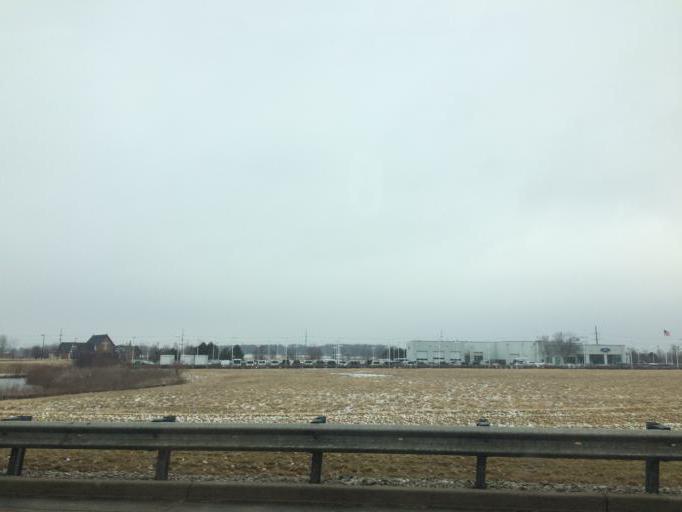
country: US
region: Illinois
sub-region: McHenry County
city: Huntley
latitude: 42.1275
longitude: -88.4326
